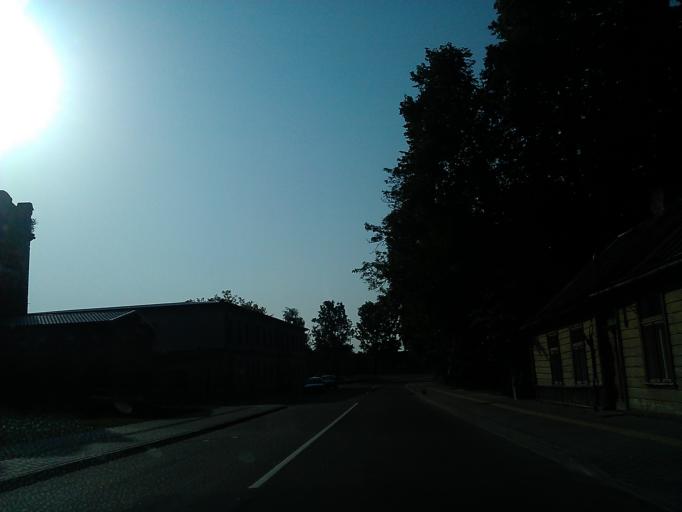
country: LV
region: Aizpute
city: Aizpute
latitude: 56.7163
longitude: 21.6134
